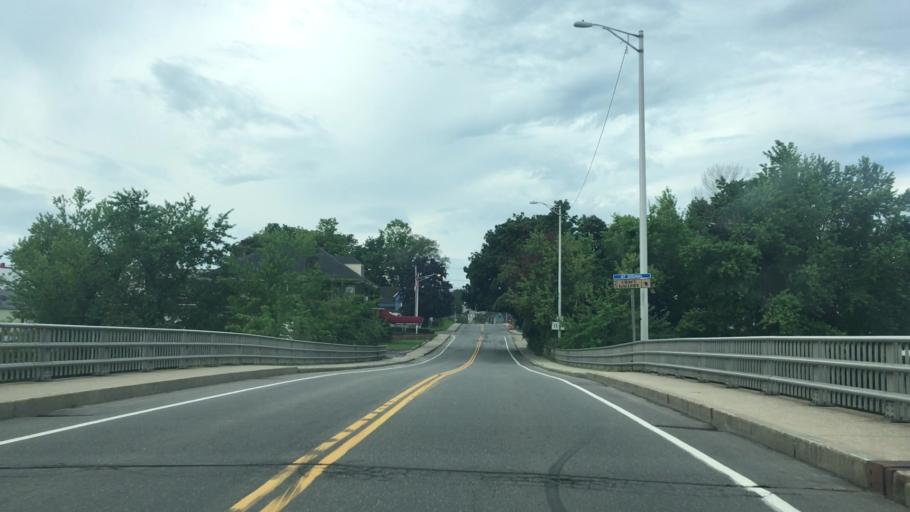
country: US
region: Maine
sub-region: York County
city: Sanford (historical)
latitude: 43.4431
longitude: -70.7754
